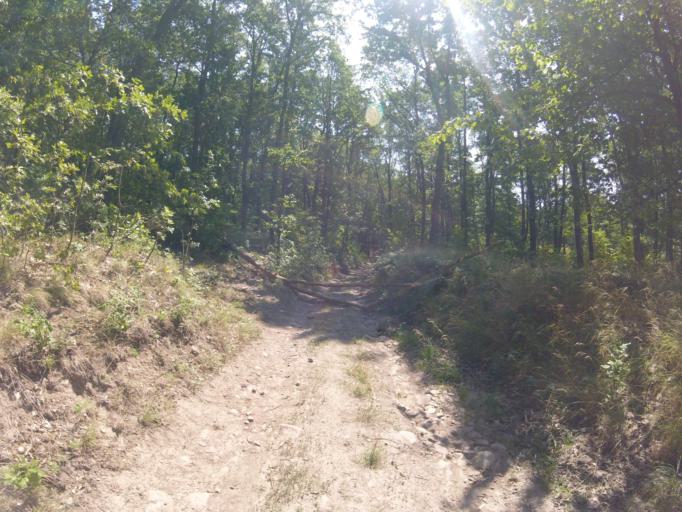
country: HU
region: Pest
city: Csobanka
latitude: 47.6787
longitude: 18.9622
